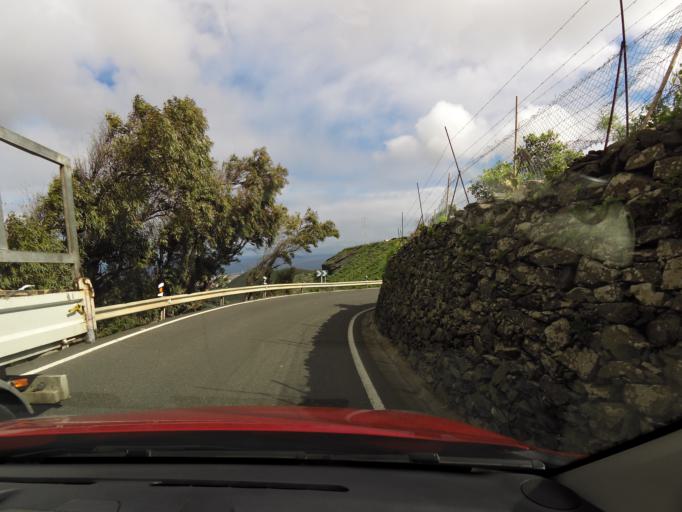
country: ES
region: Canary Islands
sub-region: Provincia de Las Palmas
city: Telde
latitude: 28.0207
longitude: -15.4567
